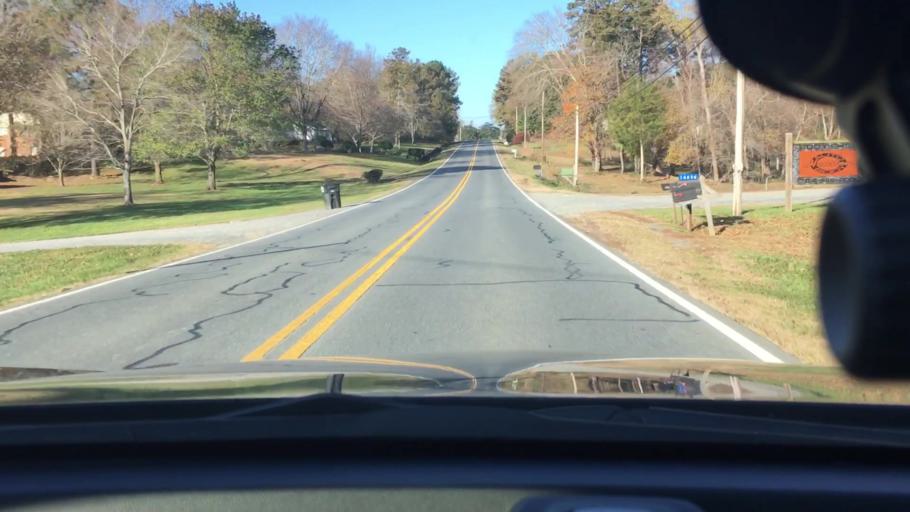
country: US
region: North Carolina
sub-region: Cabarrus County
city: Mount Pleasant
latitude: 35.3829
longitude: -80.3490
